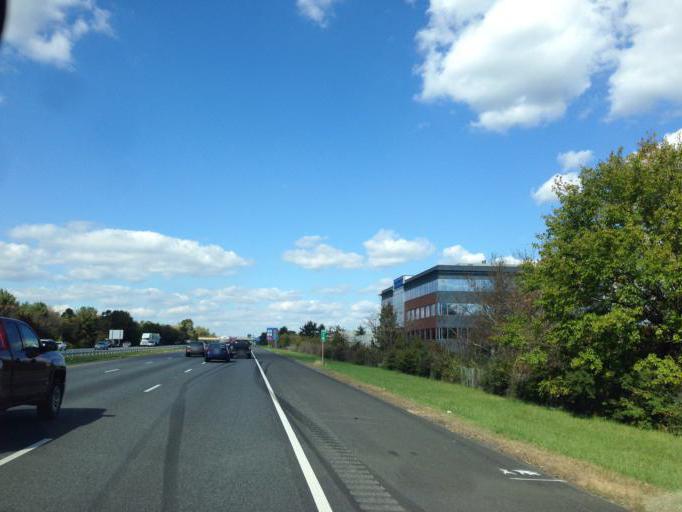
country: US
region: Maryland
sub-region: Baltimore County
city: Cockeysville
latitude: 39.4756
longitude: -76.6636
